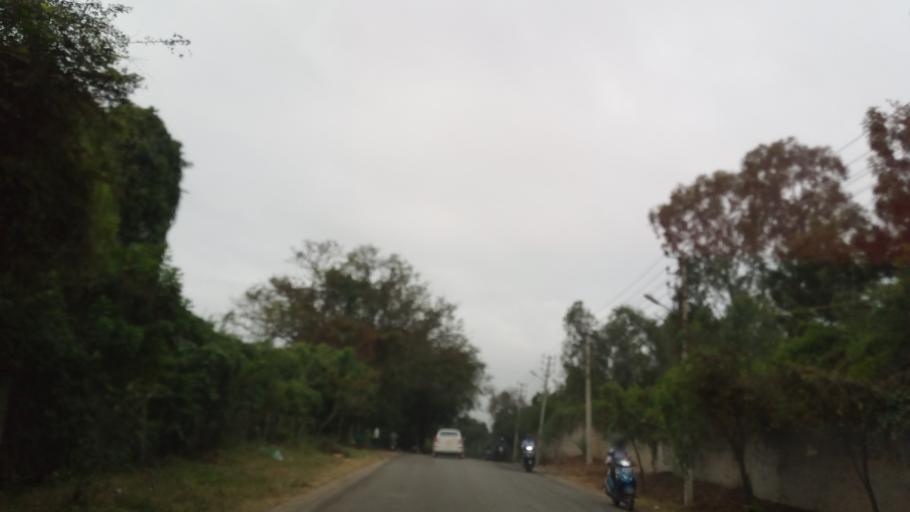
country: IN
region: Karnataka
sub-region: Bangalore Urban
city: Bangalore
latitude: 12.9082
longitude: 77.4971
